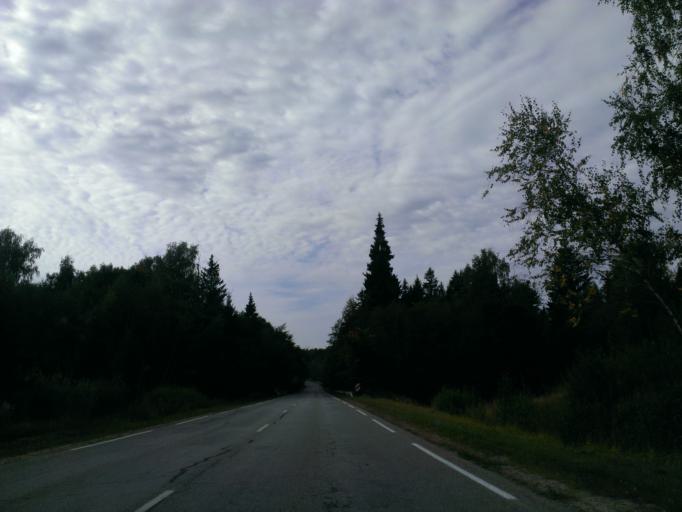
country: LV
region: Sigulda
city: Sigulda
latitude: 57.1823
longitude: 24.8281
